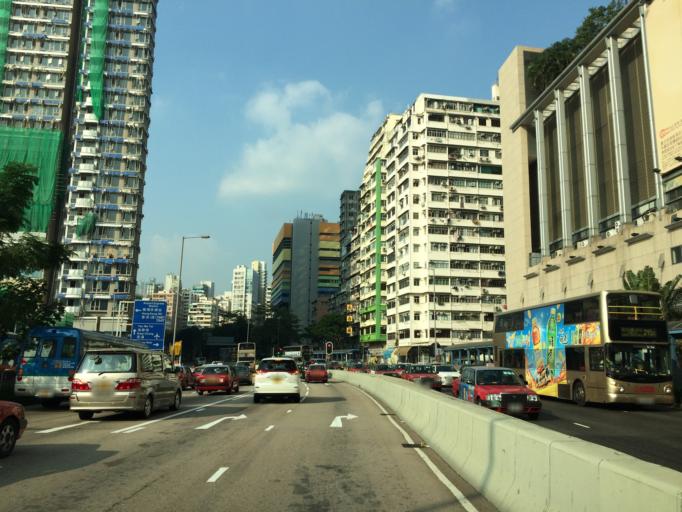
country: HK
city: Hong Kong
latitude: 22.3023
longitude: 114.1680
